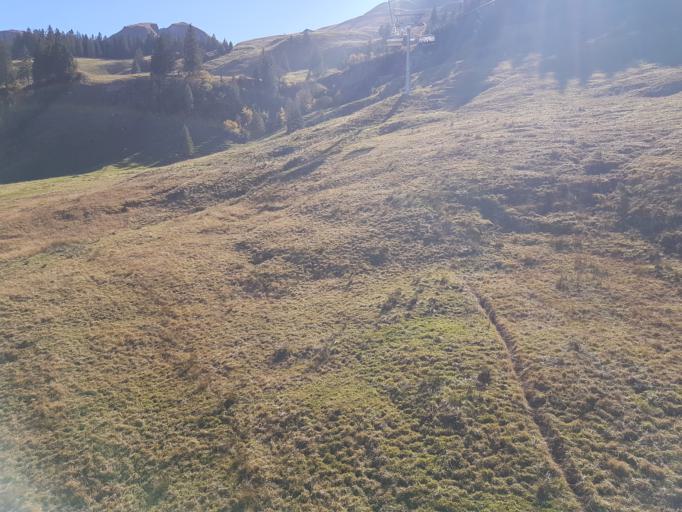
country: CH
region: Schwyz
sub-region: Bezirk Schwyz
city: Ibach
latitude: 46.9715
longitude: 8.6718
